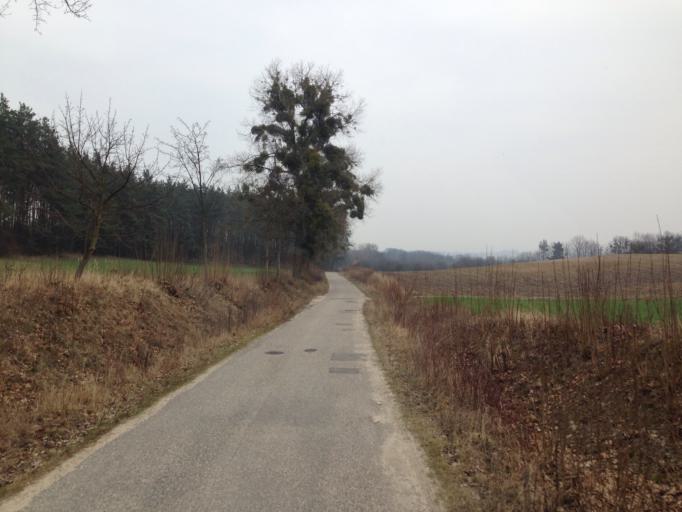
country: PL
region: Pomeranian Voivodeship
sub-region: Powiat kwidzynski
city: Sadlinki
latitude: 53.7285
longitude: 18.8202
